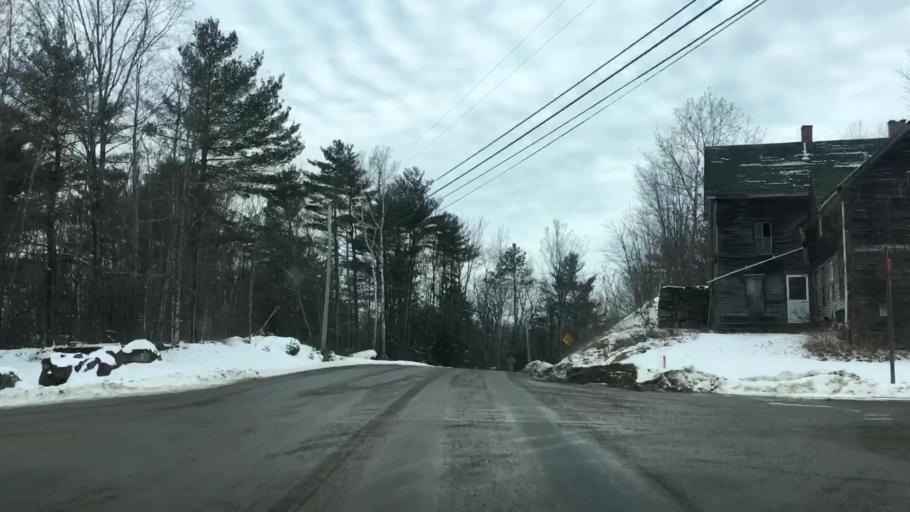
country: US
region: Maine
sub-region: Lincoln County
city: Whitefield
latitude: 44.2492
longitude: -69.6357
